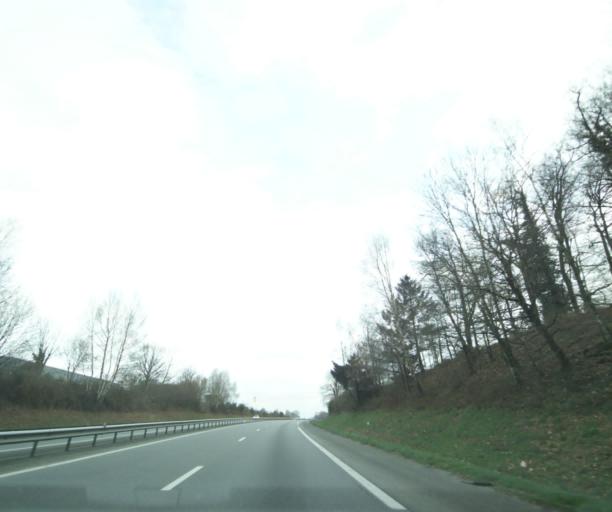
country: FR
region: Limousin
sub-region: Departement de la Haute-Vienne
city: Boisseuil
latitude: 45.7625
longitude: 1.3297
